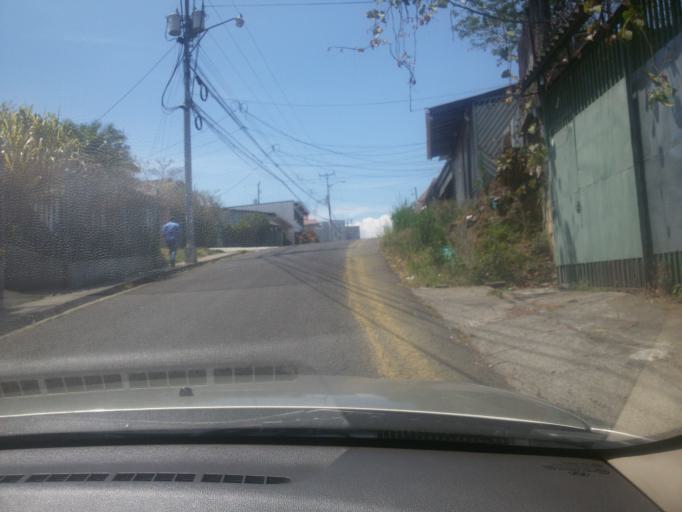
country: CR
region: San Jose
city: San Pedro
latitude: 9.9294
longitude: -84.0449
